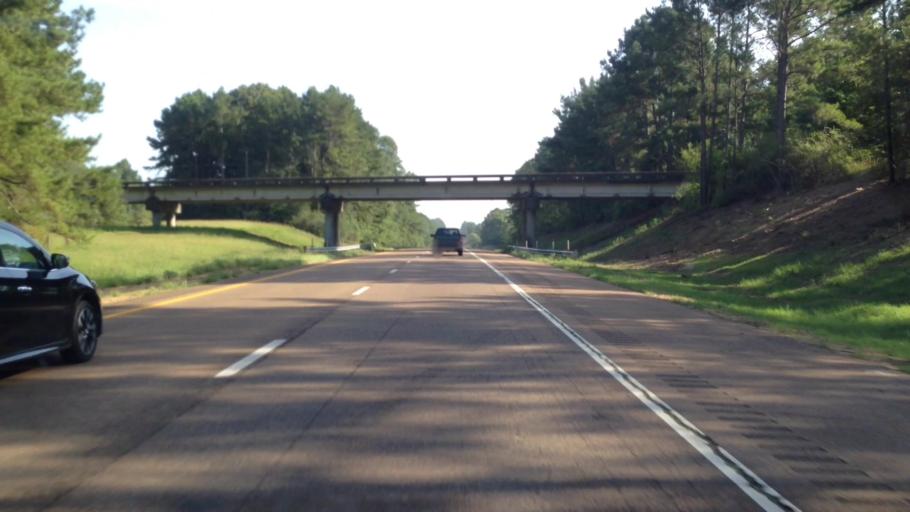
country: US
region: Mississippi
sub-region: Lincoln County
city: Brookhaven
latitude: 31.4494
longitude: -90.4792
